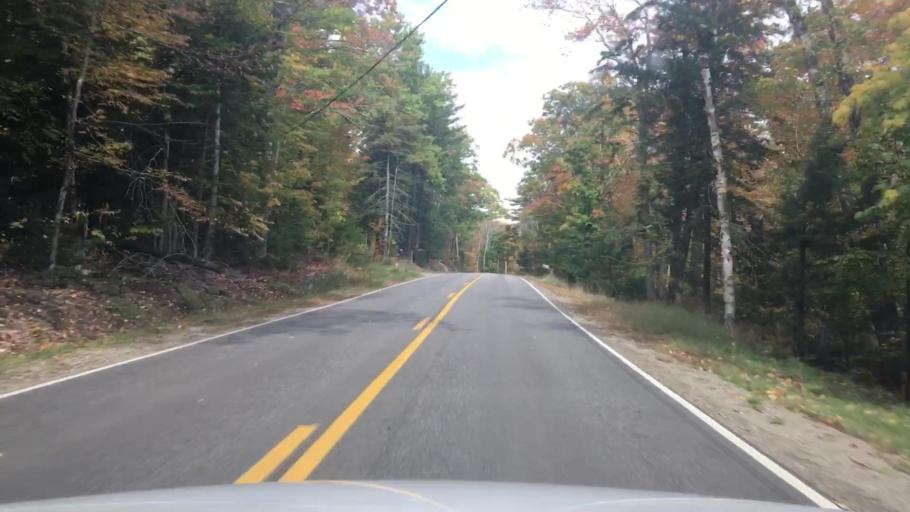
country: US
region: Maine
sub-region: Knox County
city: Hope
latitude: 44.2552
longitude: -69.1309
